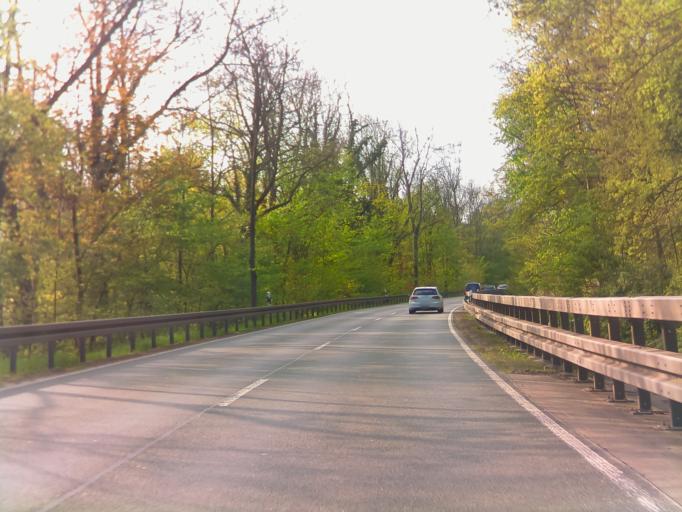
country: DE
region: Thuringia
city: Kaulsdorf
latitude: 50.6077
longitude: 11.4383
